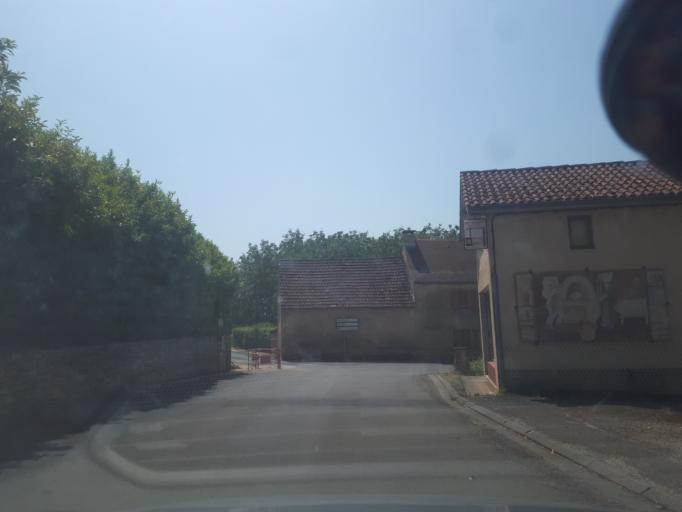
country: FR
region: Midi-Pyrenees
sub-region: Departement du Lot
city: Gourdon
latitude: 44.8339
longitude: 1.3924
